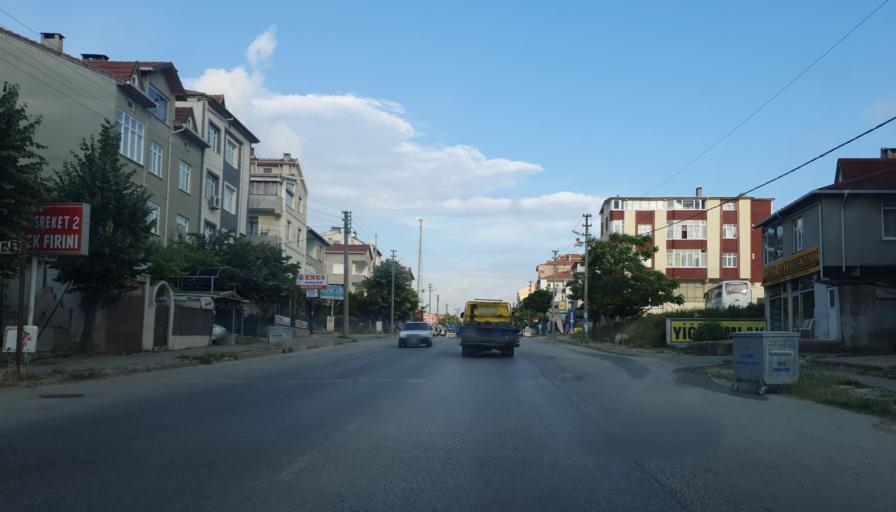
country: TR
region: Tekirdag
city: Saray
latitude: 41.3592
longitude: 27.9476
